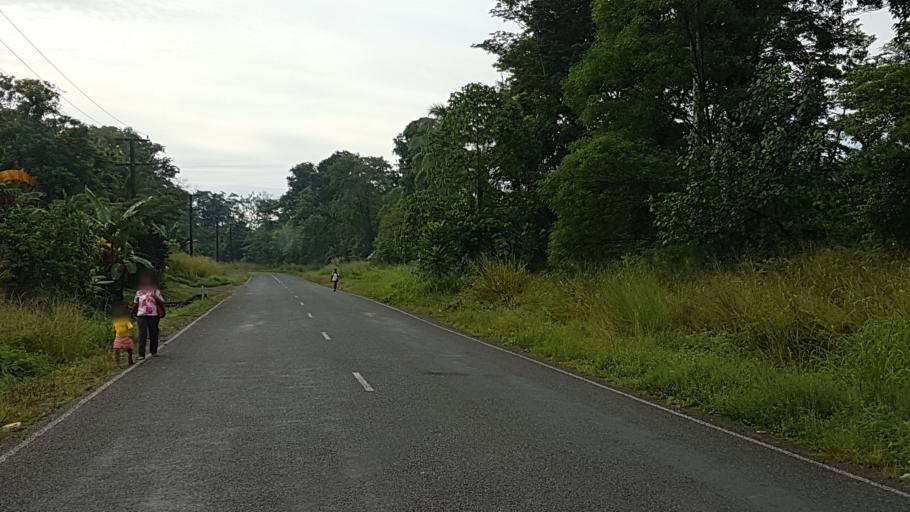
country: PG
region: Milne Bay
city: Alotau
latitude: -10.3169
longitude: 150.4714
